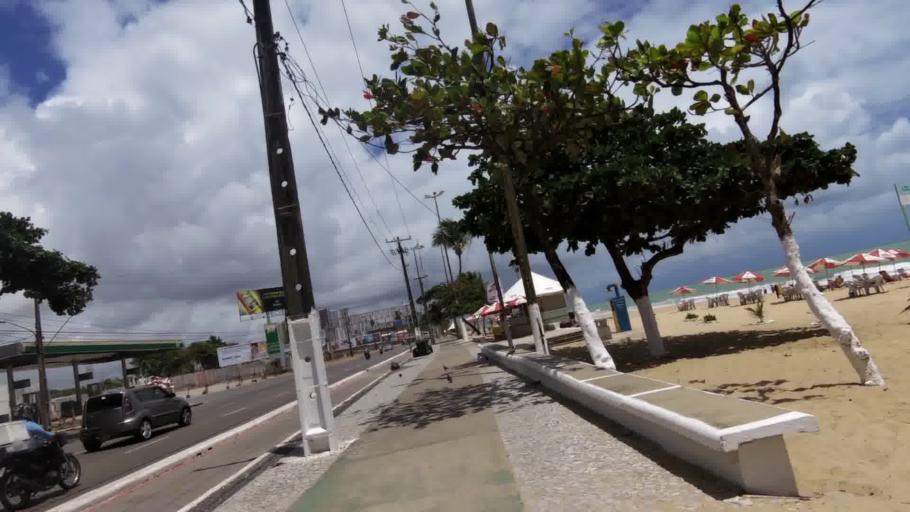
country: BR
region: Pernambuco
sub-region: Jaboatao Dos Guararapes
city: Jaboatao
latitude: -8.1558
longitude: -34.9097
